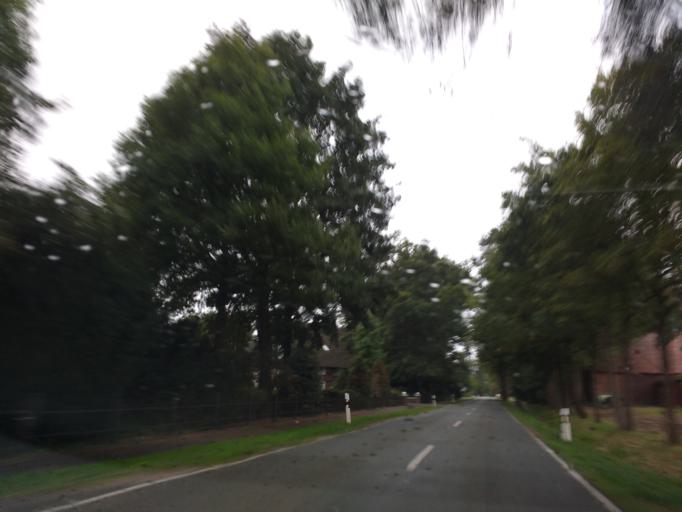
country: DE
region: North Rhine-Westphalia
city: Rietberg
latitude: 51.7389
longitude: 8.4441
